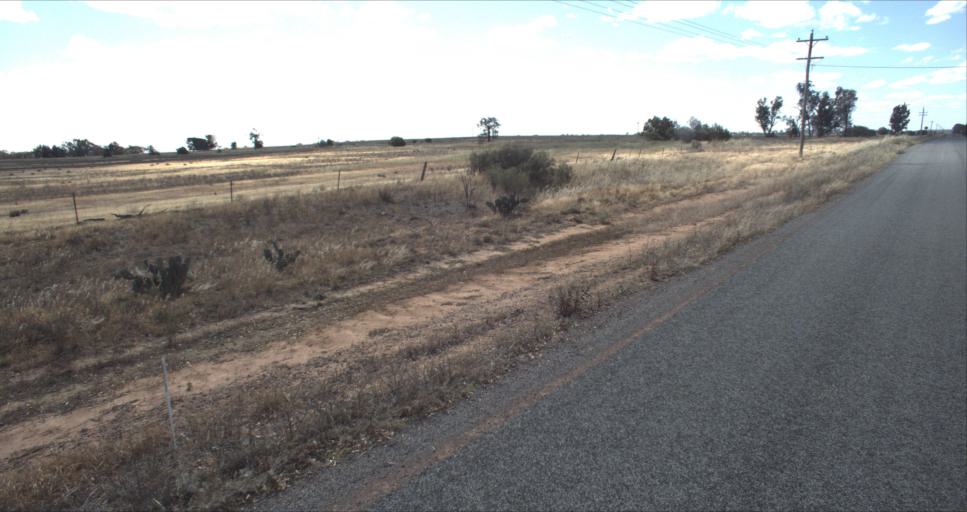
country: AU
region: New South Wales
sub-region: Leeton
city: Leeton
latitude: -34.4850
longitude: 146.2484
